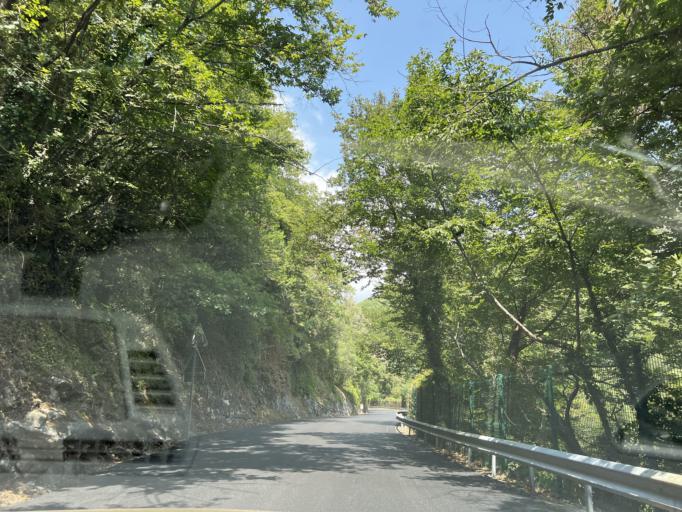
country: FR
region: Provence-Alpes-Cote d'Azur
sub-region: Departement des Alpes-Maritimes
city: Tourrettes-sur-Loup
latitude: 43.7590
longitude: 6.9902
